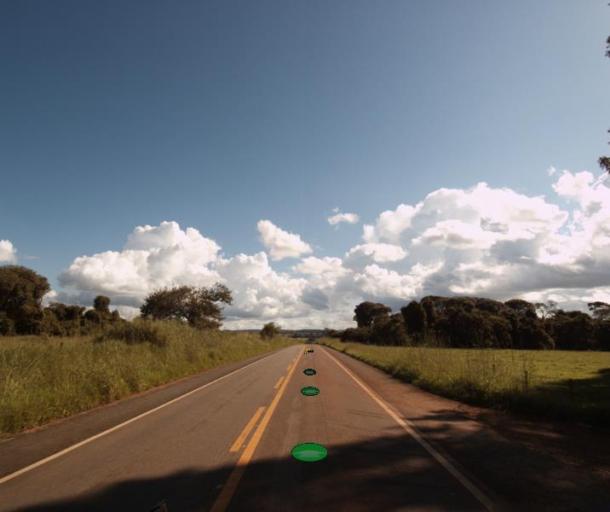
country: BR
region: Goias
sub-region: Itaberai
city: Itaberai
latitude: -15.9309
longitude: -49.6150
